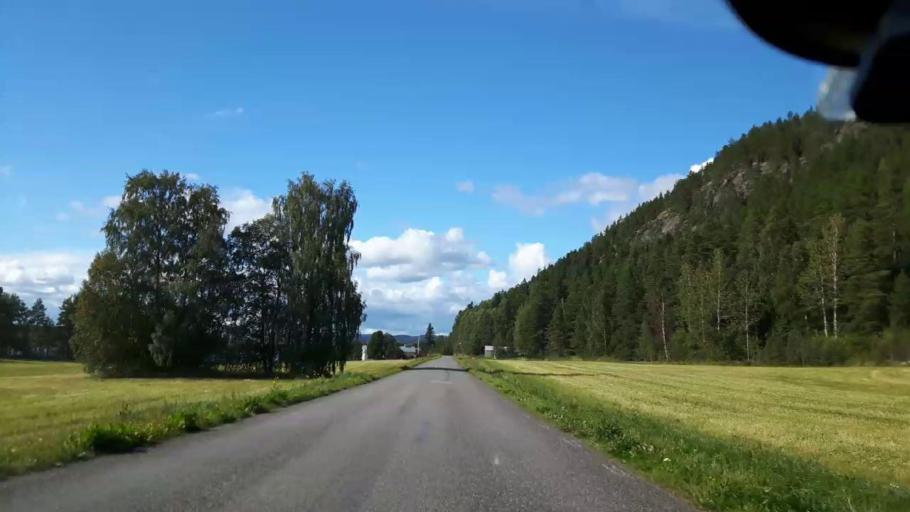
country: SE
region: Jaemtland
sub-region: Braecke Kommun
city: Braecke
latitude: 63.1702
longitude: 15.5747
